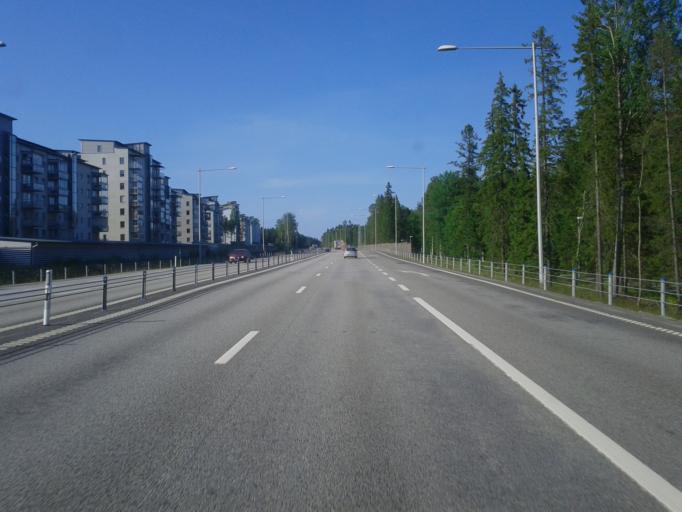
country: SE
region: Vaesterbotten
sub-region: Umea Kommun
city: Ersmark
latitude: 63.8344
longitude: 20.3341
